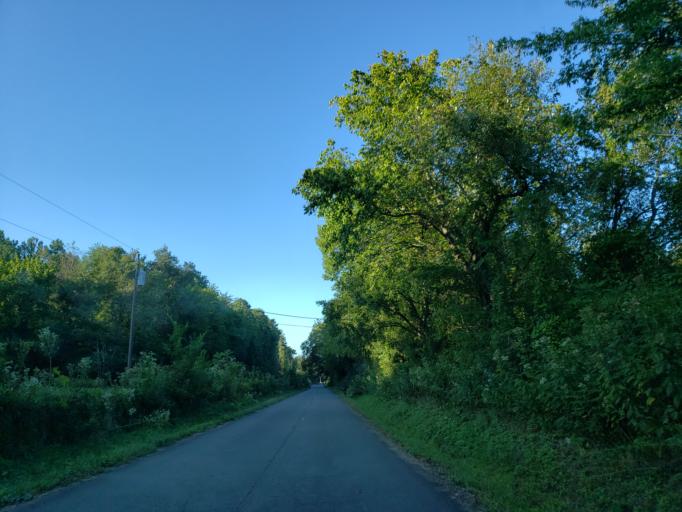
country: US
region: Georgia
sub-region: Bartow County
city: Rydal
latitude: 34.3099
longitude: -84.7329
